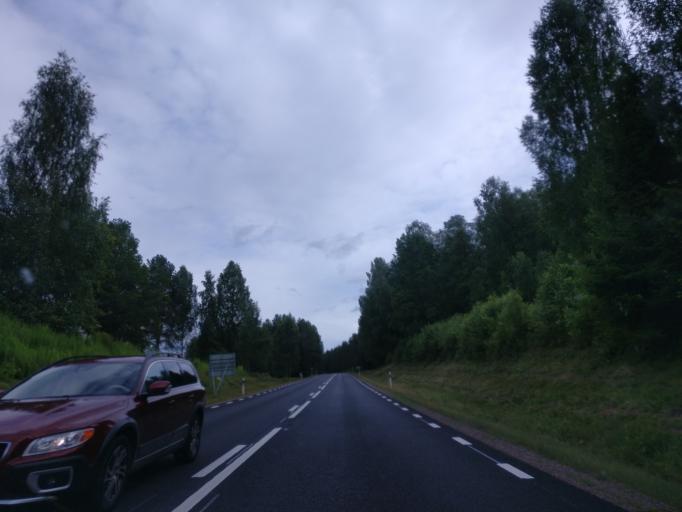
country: SE
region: Vaermland
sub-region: Hagfors Kommun
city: Hagfors
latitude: 60.0596
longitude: 13.5526
